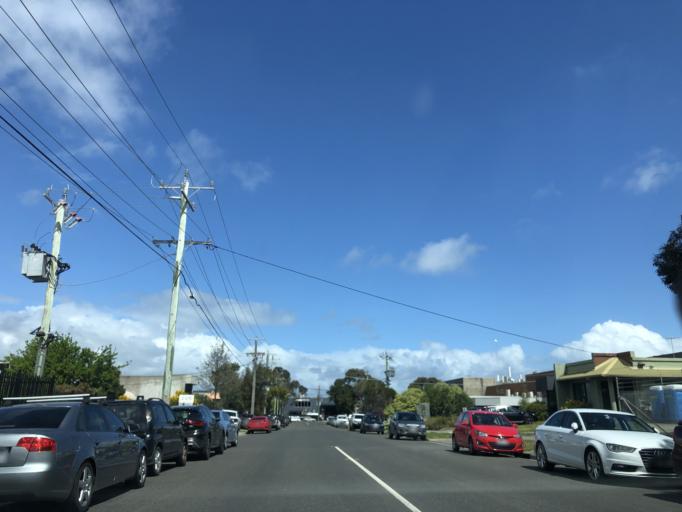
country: AU
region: Victoria
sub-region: Monash
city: Oakleigh South
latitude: -37.9296
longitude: 145.0980
